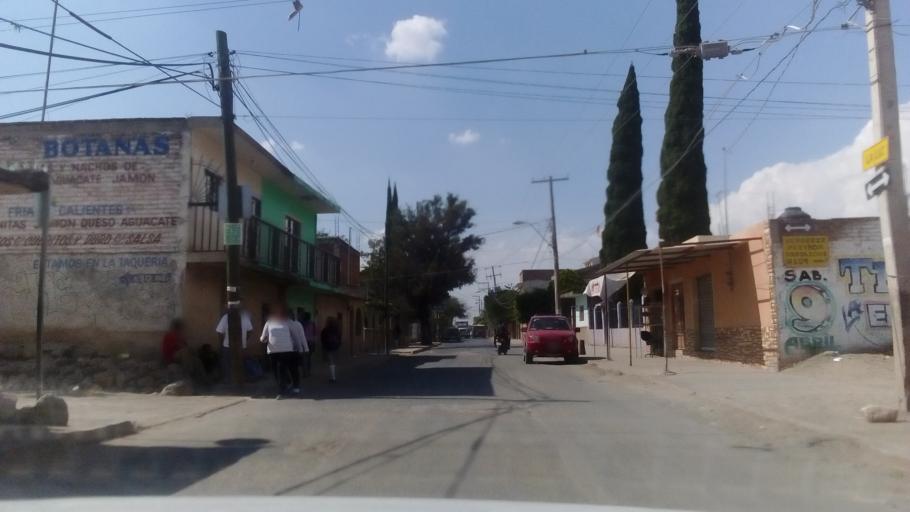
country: MX
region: Guanajuato
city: Duarte
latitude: 21.0876
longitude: -101.5252
